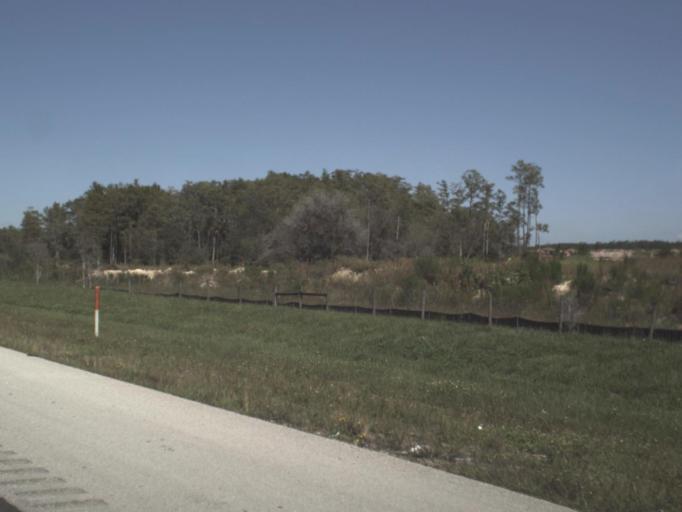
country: US
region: Florida
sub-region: Lee County
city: Gateway
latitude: 26.5704
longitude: -81.7923
